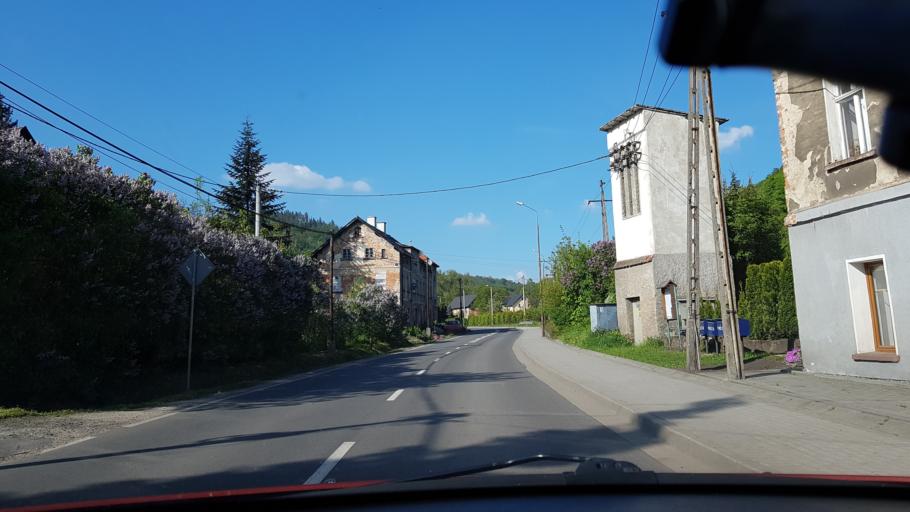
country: PL
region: Lower Silesian Voivodeship
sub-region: Powiat klodzki
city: Nowa Ruda
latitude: 50.5715
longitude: 16.4737
